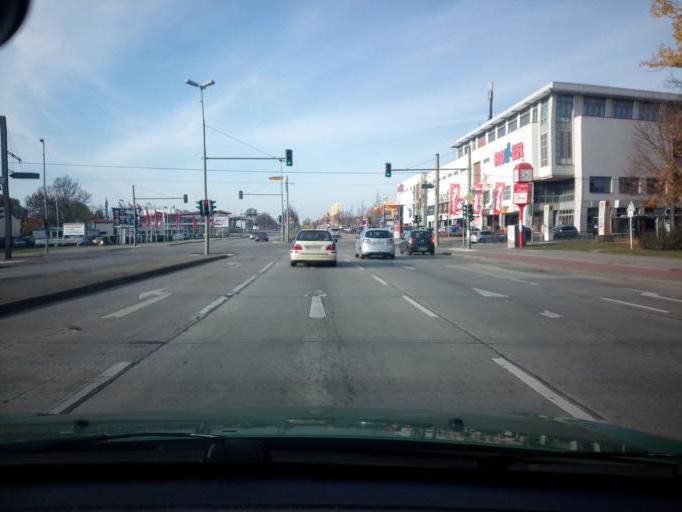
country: DE
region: Berlin
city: Mahlsdorf
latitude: 52.5049
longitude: 13.6143
